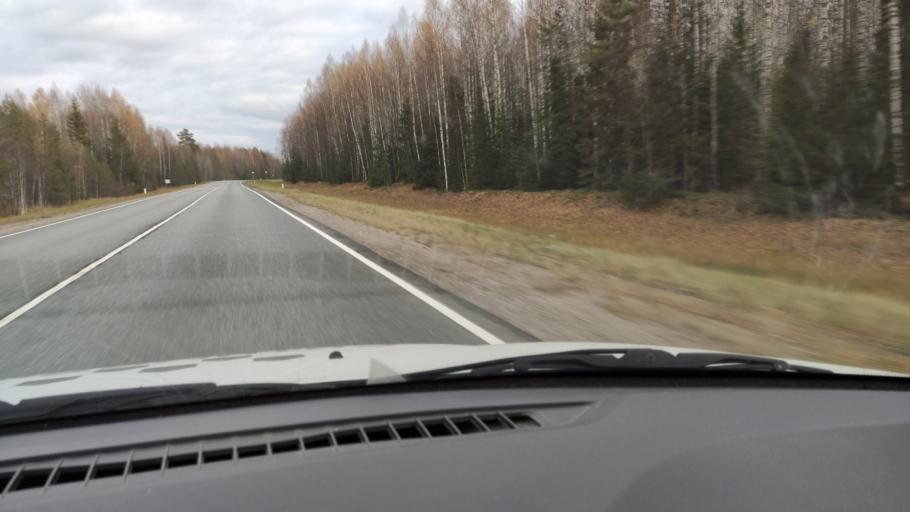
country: RU
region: Kirov
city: Dubrovka
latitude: 58.8983
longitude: 51.3134
